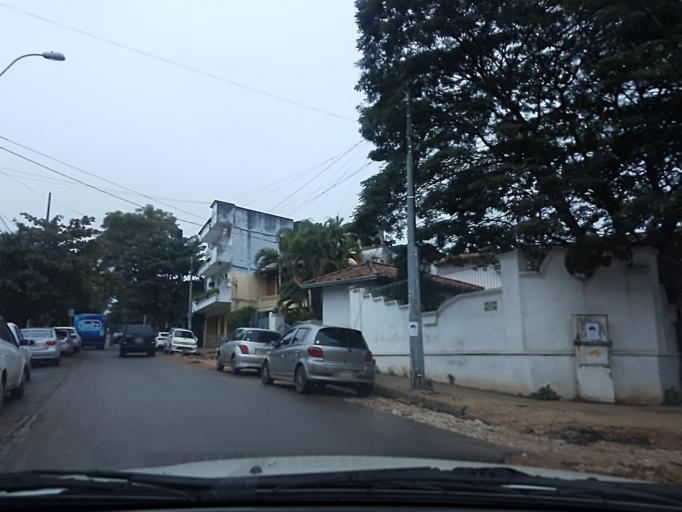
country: PY
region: Asuncion
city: Asuncion
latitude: -25.2817
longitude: -57.6121
